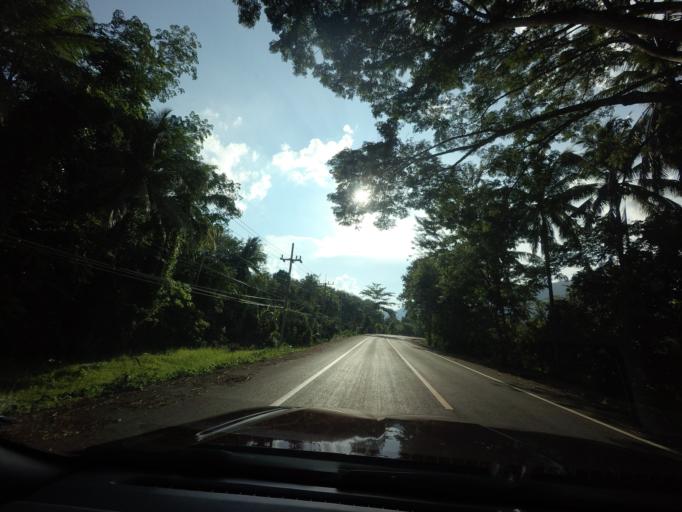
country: TH
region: Yala
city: Ban Nang Sata
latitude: 6.2244
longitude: 101.2237
